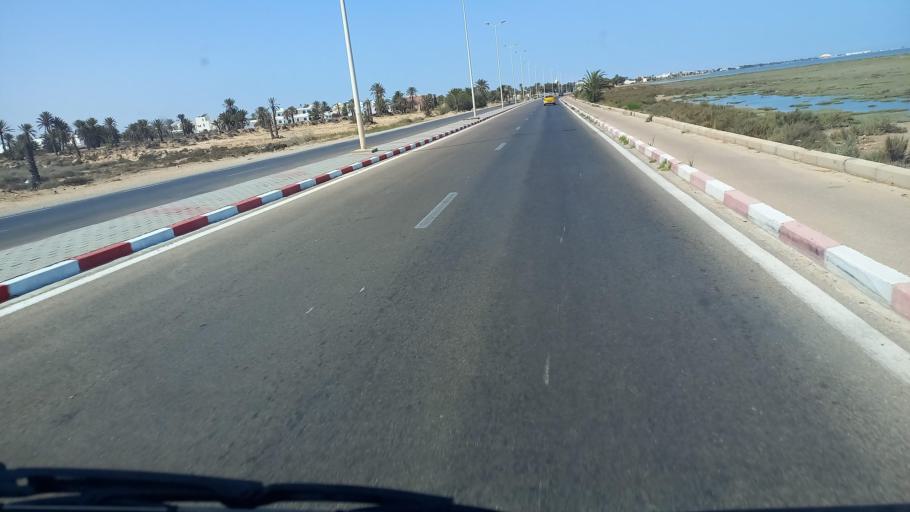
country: TN
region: Madanin
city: Houmt Souk
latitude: 33.8738
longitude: 10.9198
